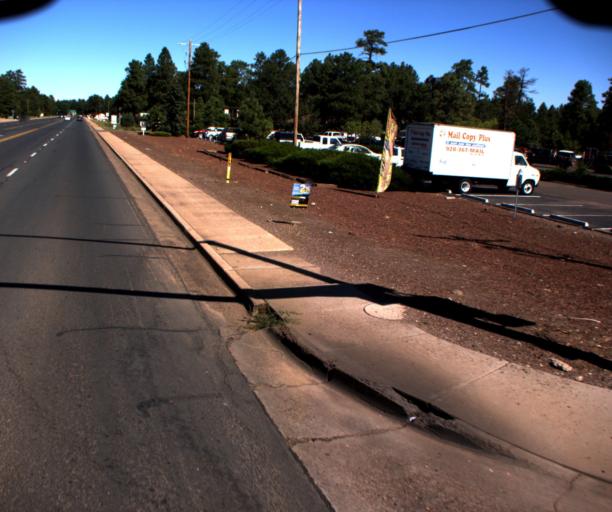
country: US
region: Arizona
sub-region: Navajo County
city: Pinetop-Lakeside
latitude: 34.1421
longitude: -109.9551
